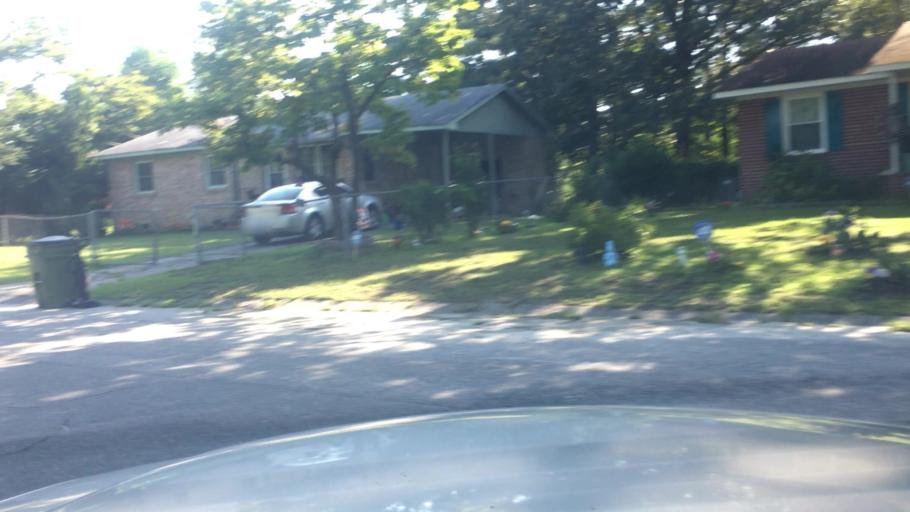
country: US
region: North Carolina
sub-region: Cumberland County
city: Spring Lake
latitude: 35.1515
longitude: -78.9184
